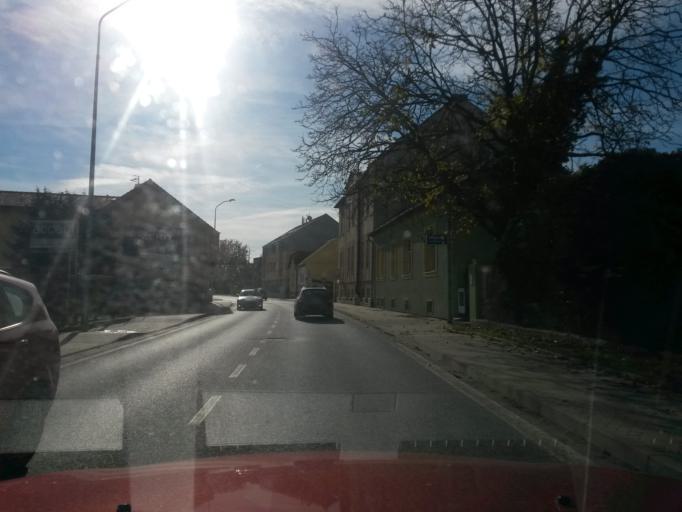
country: SK
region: Presovsky
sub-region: Okres Presov
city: Presov
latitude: 48.9987
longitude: 21.2355
